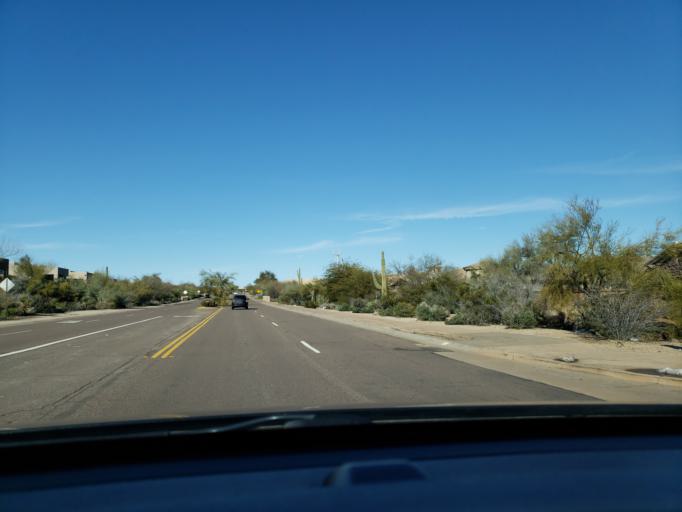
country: US
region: Arizona
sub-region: Maricopa County
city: Carefree
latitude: 33.7353
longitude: -111.8466
